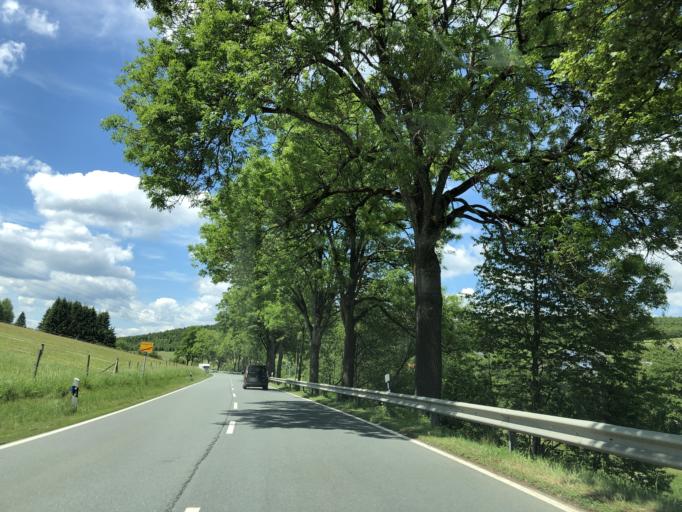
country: DE
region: North Rhine-Westphalia
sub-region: Regierungsbezirk Arnsberg
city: Erndtebruck
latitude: 51.0000
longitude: 8.2907
